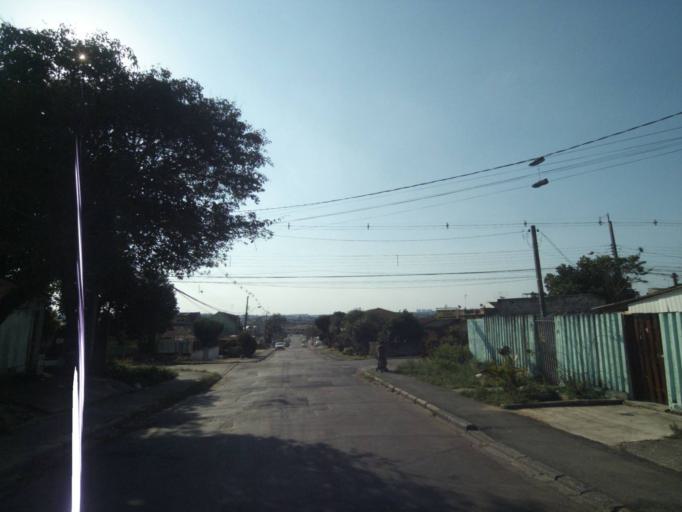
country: BR
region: Parana
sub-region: Curitiba
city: Curitiba
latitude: -25.4853
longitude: -49.3292
